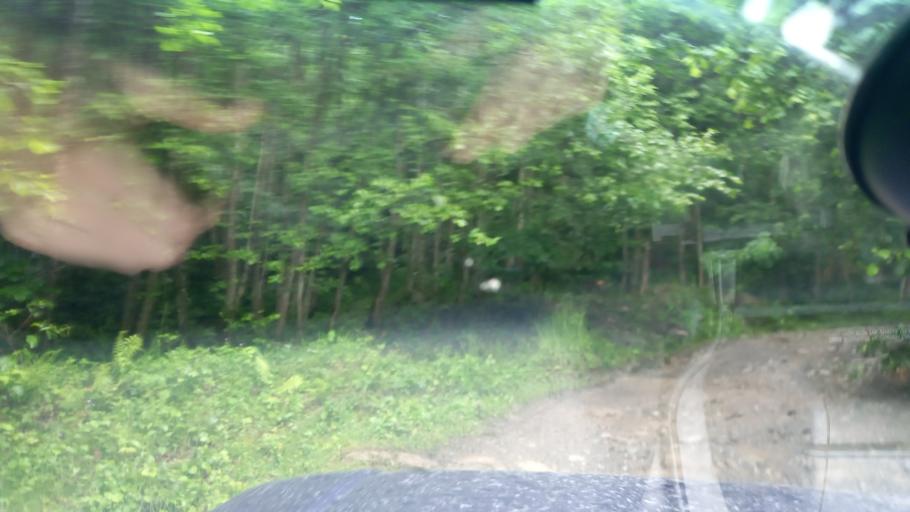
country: RU
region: Krasnodarskiy
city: Psebay
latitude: 44.0157
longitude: 40.7112
